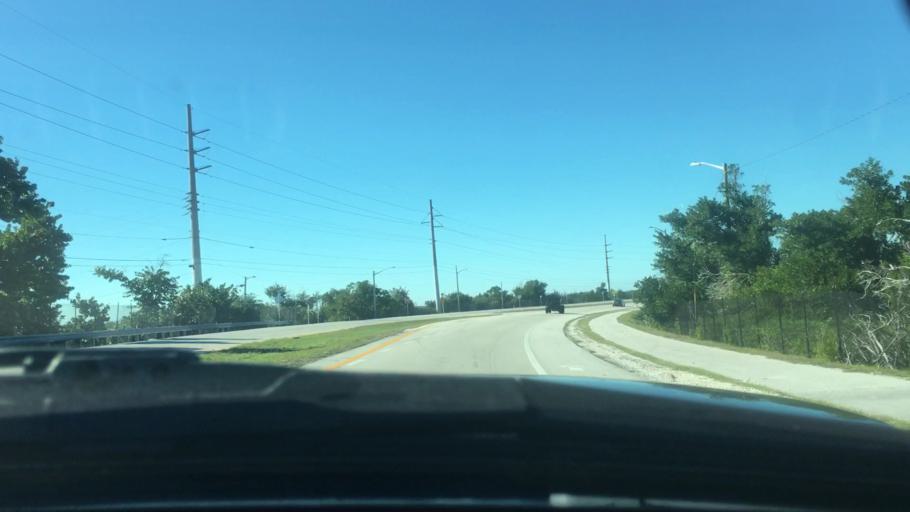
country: US
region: Florida
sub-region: Monroe County
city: Big Pine Key
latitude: 24.6483
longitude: -81.3309
